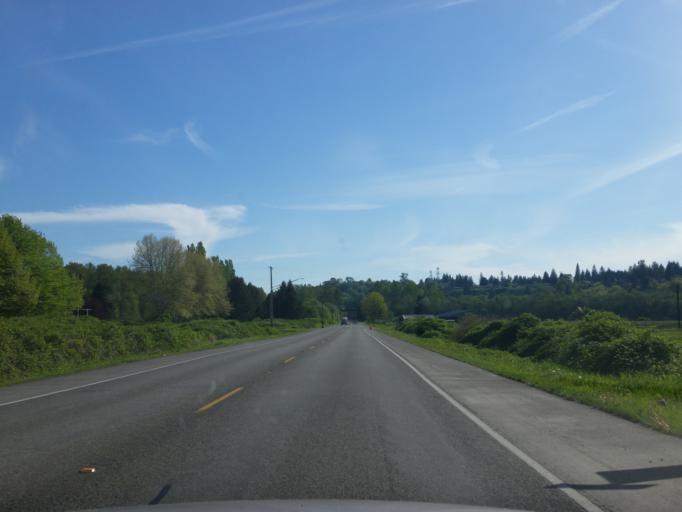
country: US
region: Washington
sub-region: Snohomish County
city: Machias
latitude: 47.9504
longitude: -122.0730
